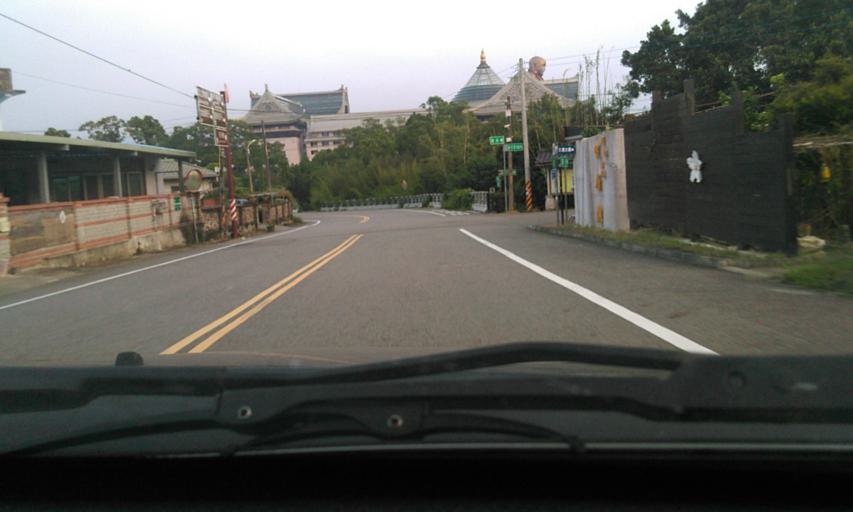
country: TW
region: Taiwan
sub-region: Hsinchu
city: Hsinchu
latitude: 24.6852
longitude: 120.9845
